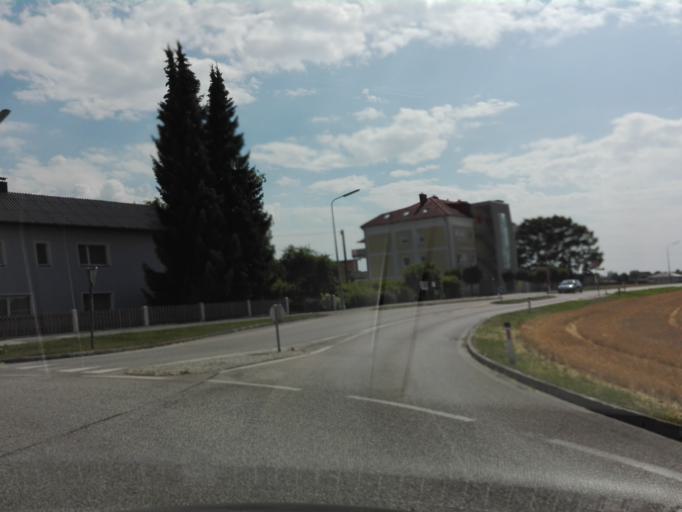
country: AT
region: Upper Austria
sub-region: Politischer Bezirk Linz-Land
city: Traun
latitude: 48.2160
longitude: 14.2191
